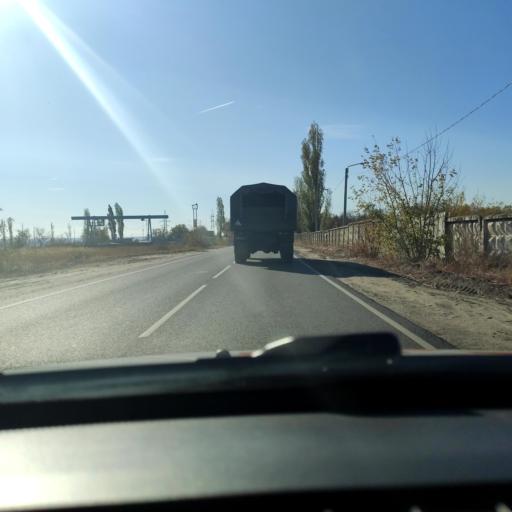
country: RU
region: Voronezj
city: Shilovo
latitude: 51.5651
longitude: 39.1403
